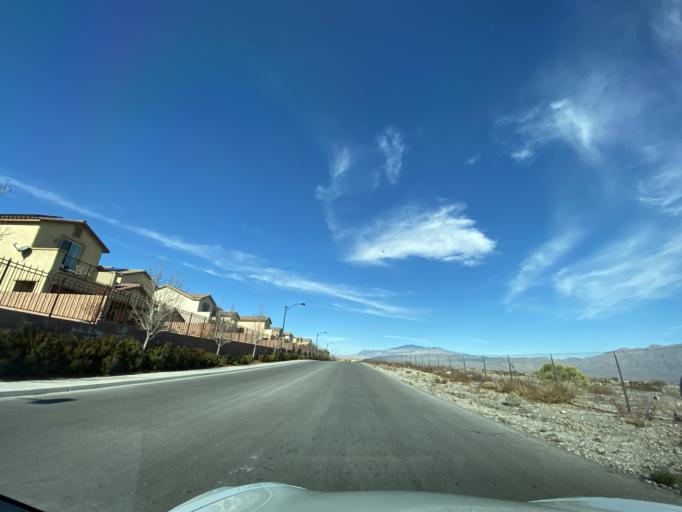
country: US
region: Nevada
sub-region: Clark County
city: Summerlin South
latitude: 36.2961
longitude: -115.3265
